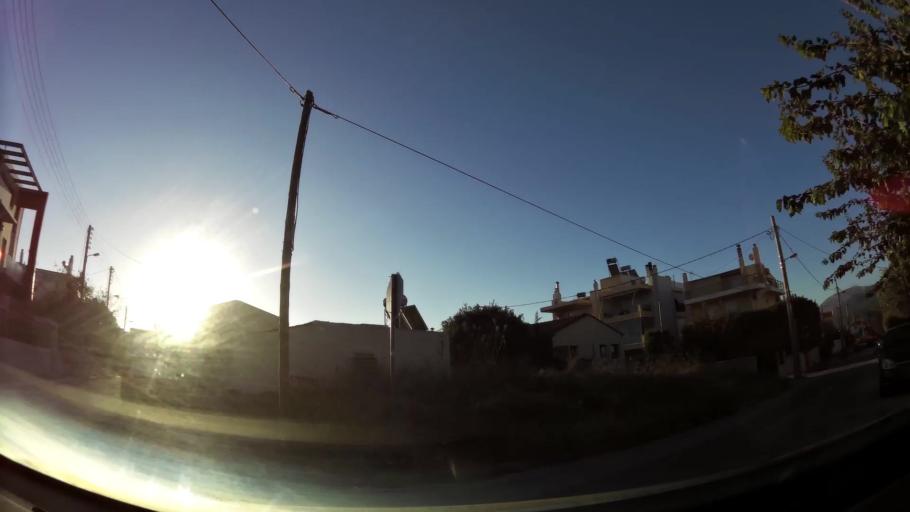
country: GR
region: Attica
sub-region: Nomarchia Anatolikis Attikis
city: Gerakas
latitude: 38.0333
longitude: 23.8554
